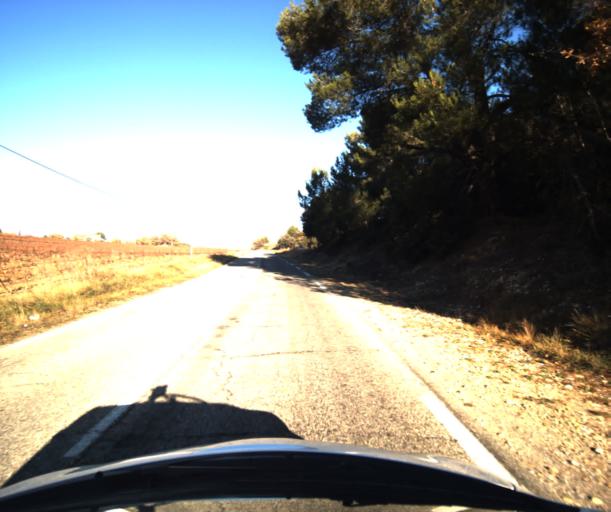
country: FR
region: Provence-Alpes-Cote d'Azur
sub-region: Departement du Vaucluse
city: Pertuis
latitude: 43.7229
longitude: 5.4994
